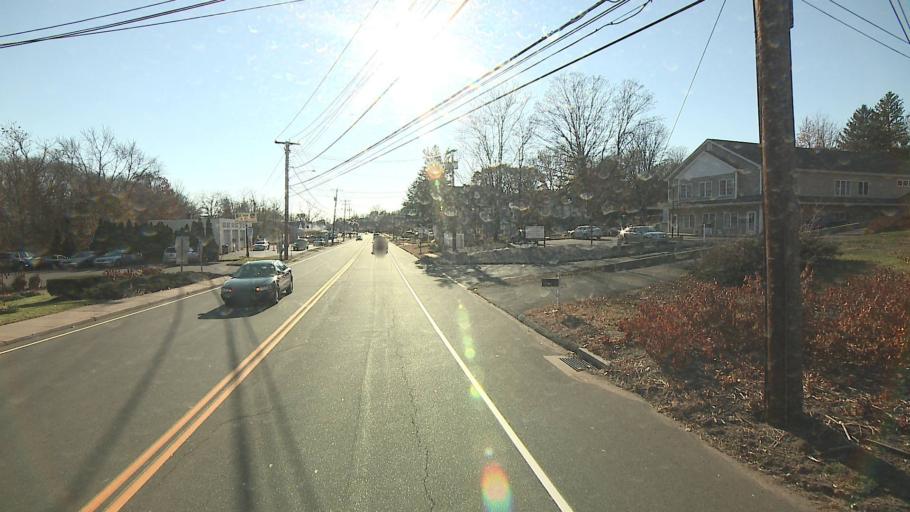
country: US
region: Connecticut
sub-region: New Haven County
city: North Haven
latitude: 41.3899
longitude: -72.8723
